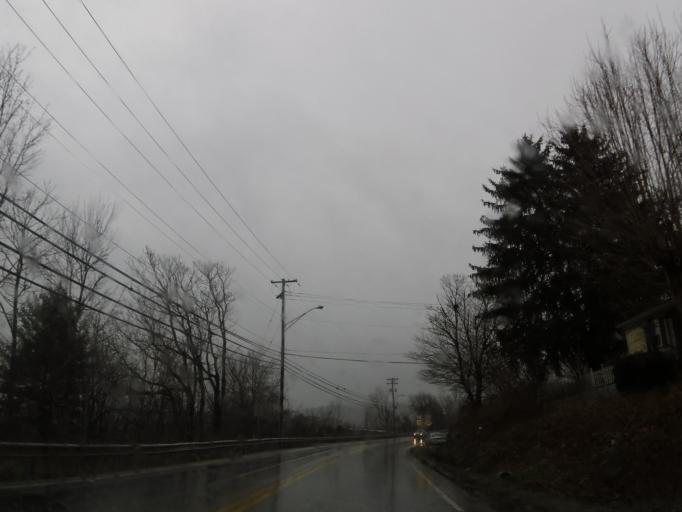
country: US
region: Kentucky
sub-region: Rockcastle County
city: Mount Vernon
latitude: 37.3531
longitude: -84.3433
